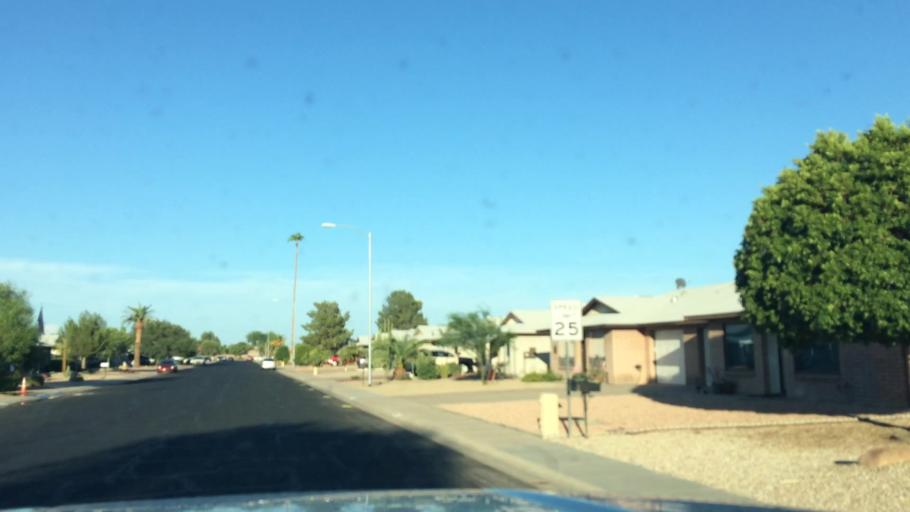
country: US
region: Arizona
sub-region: Maricopa County
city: Sun City
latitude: 33.5729
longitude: -112.2682
